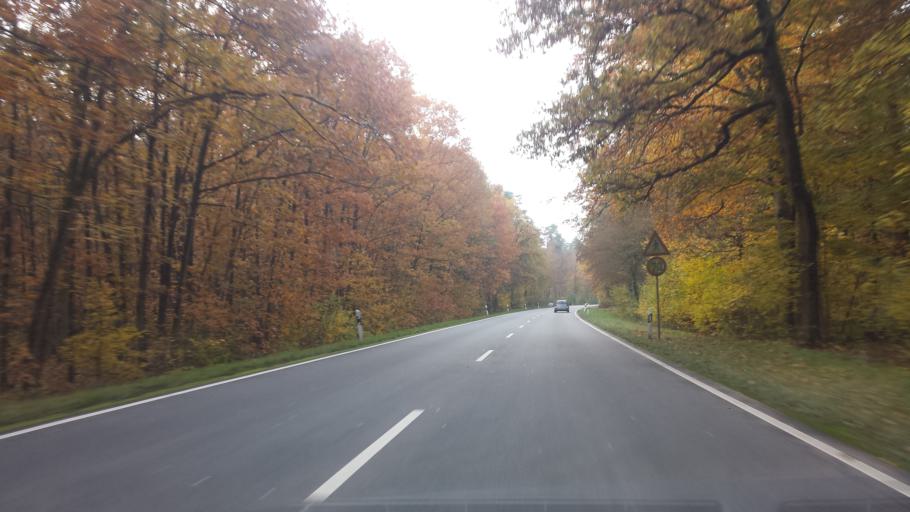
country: DE
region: Baden-Wuerttemberg
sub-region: Karlsruhe Region
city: Sandhausen
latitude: 49.3290
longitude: 8.6581
